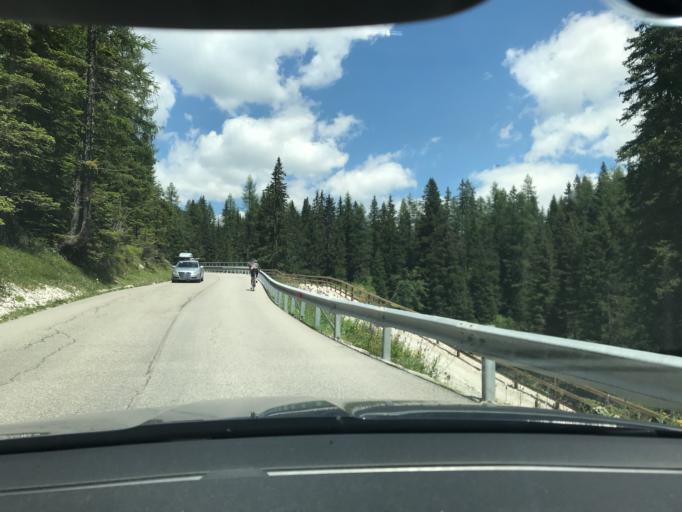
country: IT
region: Veneto
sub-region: Provincia di Belluno
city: Cortina d'Ampezzo
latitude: 46.5678
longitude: 12.2457
